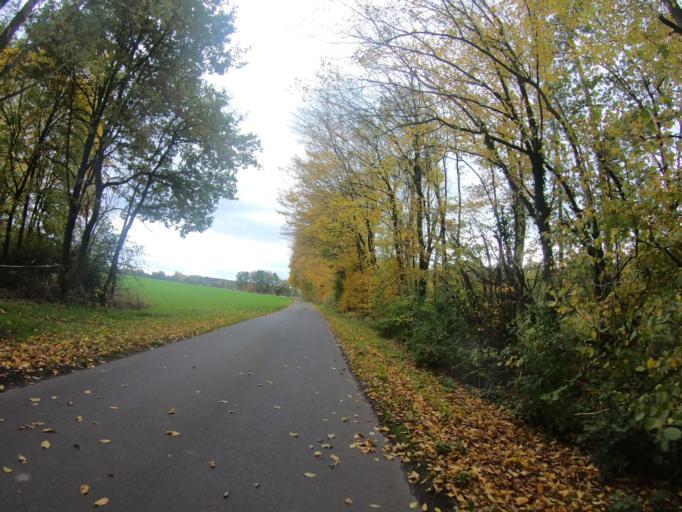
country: DE
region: Lower Saxony
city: Adenbuettel
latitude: 52.3930
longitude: 10.4820
